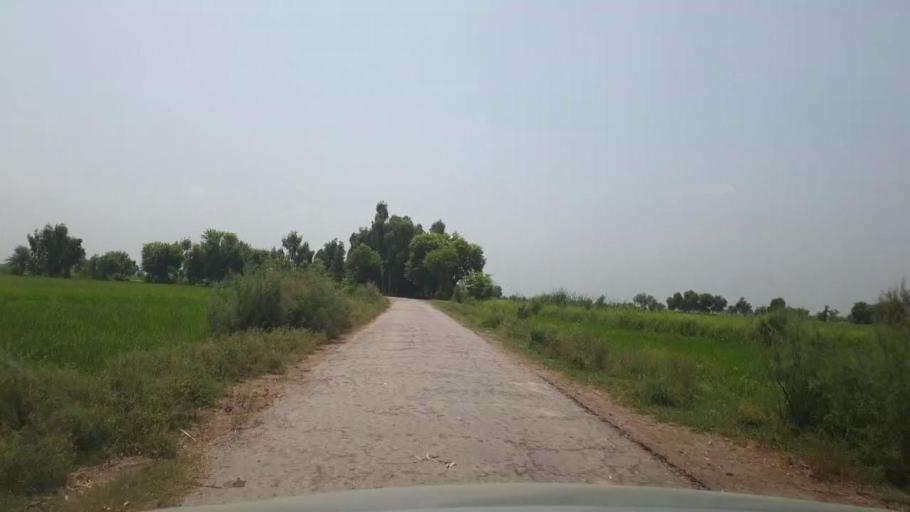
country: PK
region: Sindh
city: Garhi Yasin
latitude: 27.9432
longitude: 68.3760
